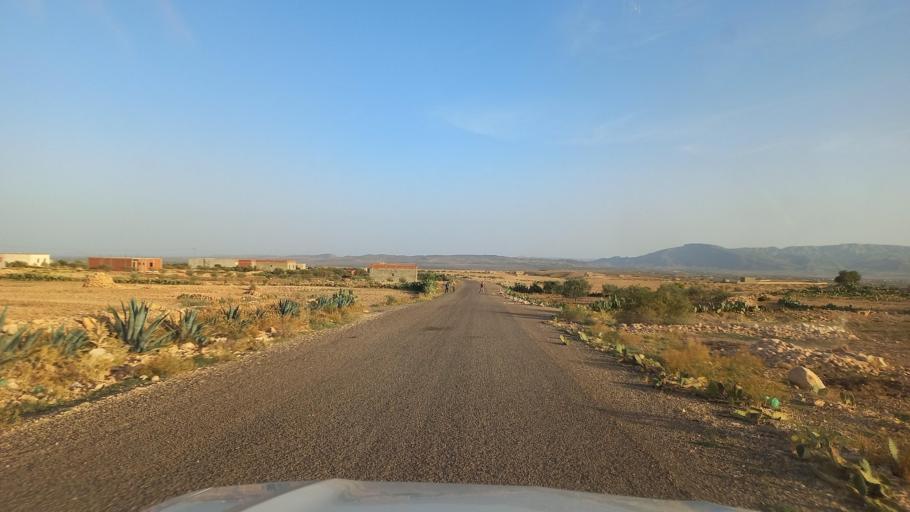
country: TN
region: Al Qasrayn
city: Kasserine
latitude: 35.2779
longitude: 8.9101
